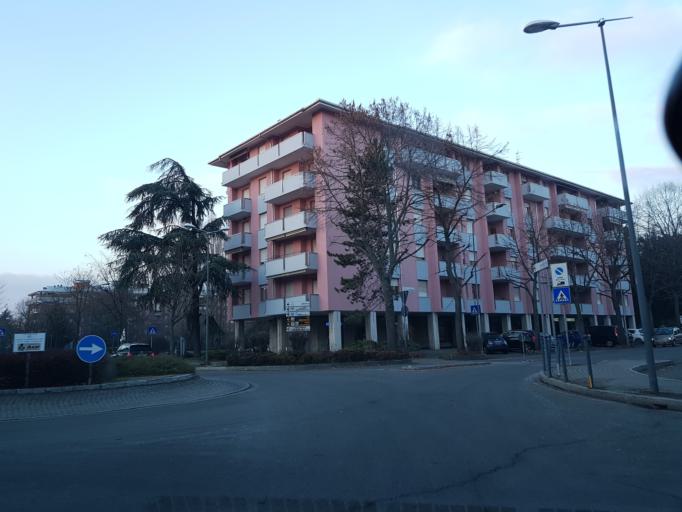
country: IT
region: Piedmont
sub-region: Provincia di Alessandria
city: Novi Ligure
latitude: 44.7637
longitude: 8.7825
